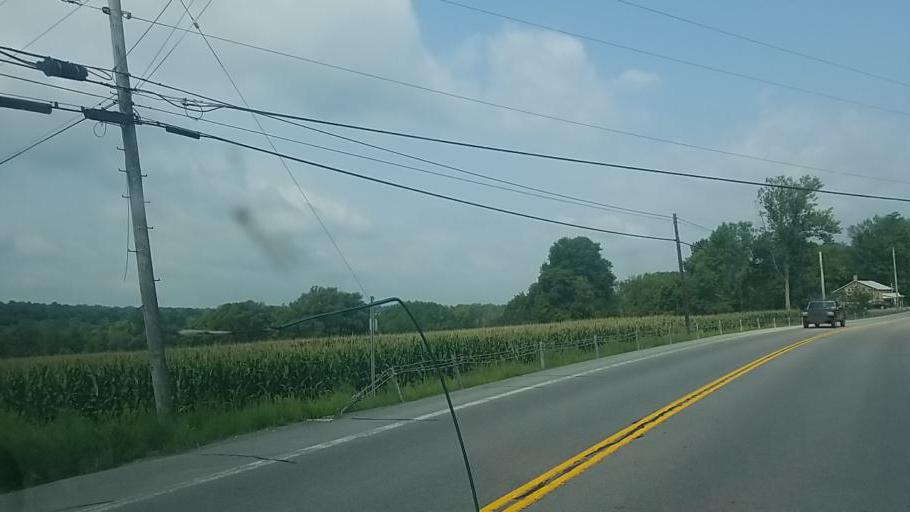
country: US
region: New York
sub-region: Montgomery County
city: Fort Plain
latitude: 42.9760
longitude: -74.6365
